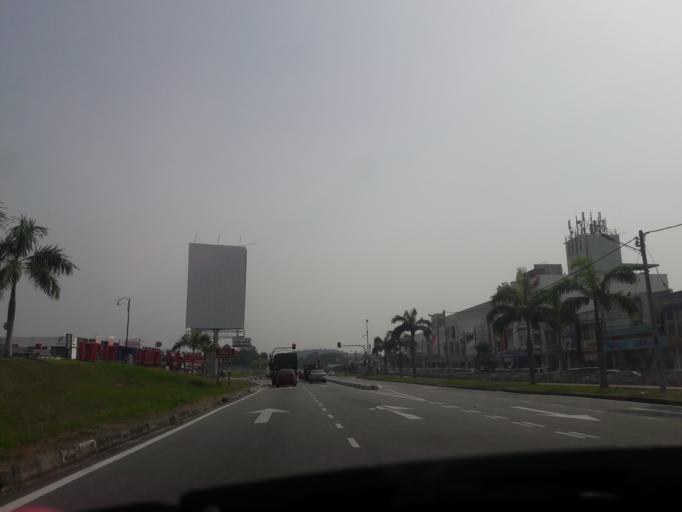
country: MY
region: Kedah
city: Kulim
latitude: 5.3838
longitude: 100.5455
